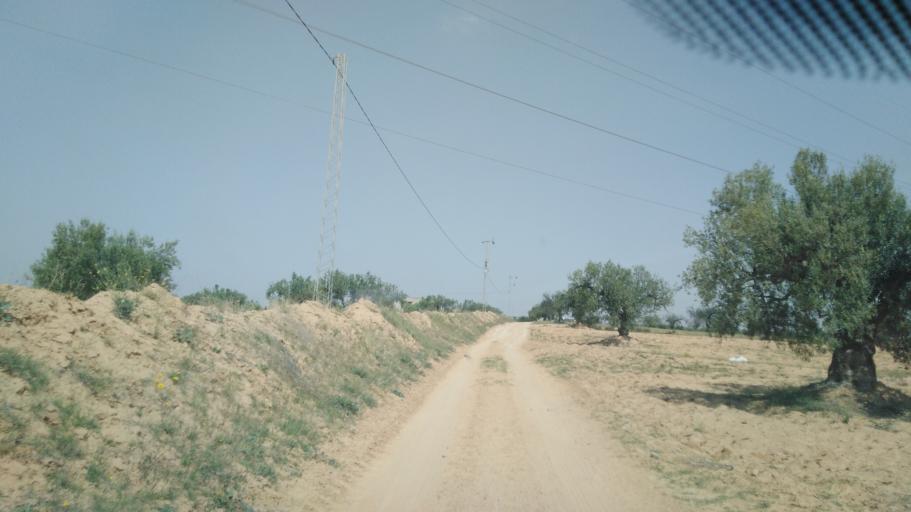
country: TN
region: Safaqis
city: Sfax
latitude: 34.7415
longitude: 10.5712
